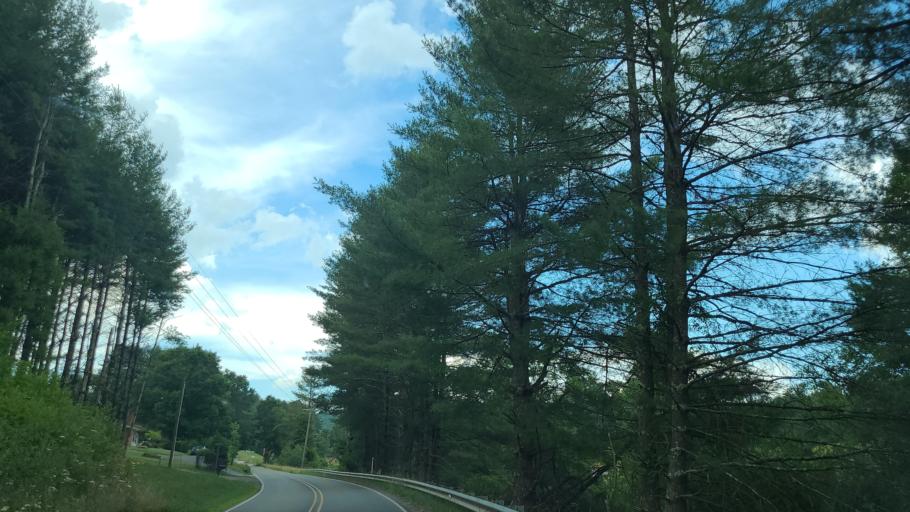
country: US
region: North Carolina
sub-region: Ashe County
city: Jefferson
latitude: 36.3899
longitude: -81.3615
